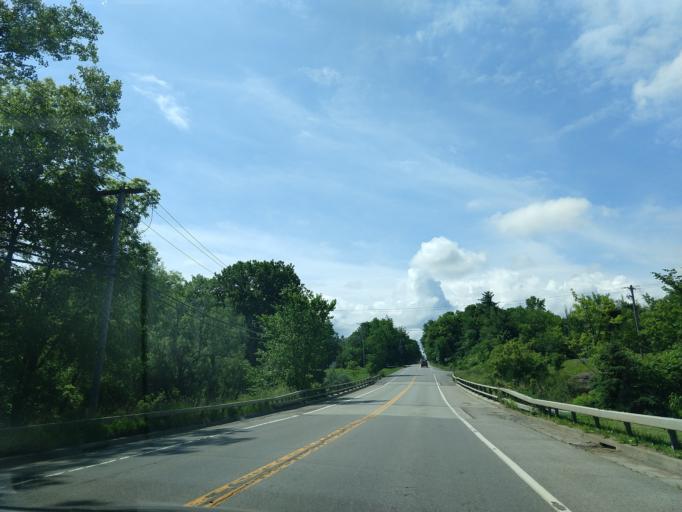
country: US
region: New York
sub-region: Erie County
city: East Aurora
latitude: 42.7580
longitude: -78.6259
